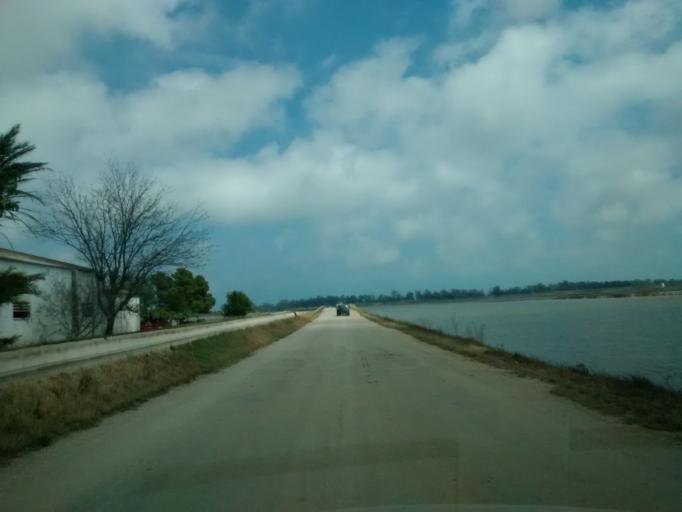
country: ES
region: Catalonia
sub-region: Provincia de Tarragona
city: Deltebre
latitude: 40.6992
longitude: 0.8111
